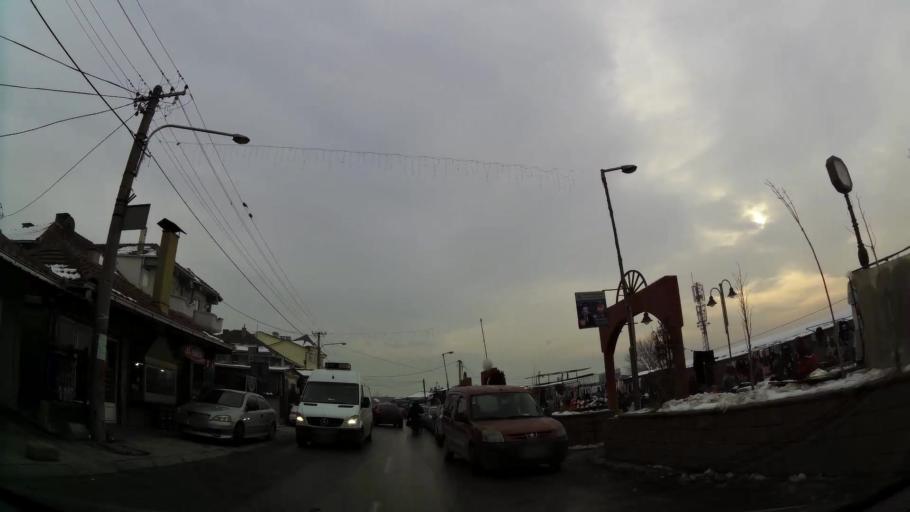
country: MK
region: Suto Orizari
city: Suto Orizare
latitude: 42.0415
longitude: 21.4238
